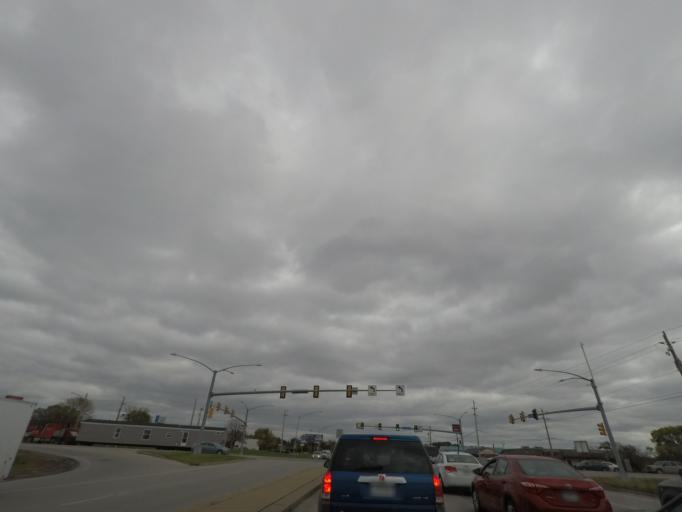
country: US
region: Iowa
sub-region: Polk County
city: Des Moines
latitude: 41.5263
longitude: -93.5975
